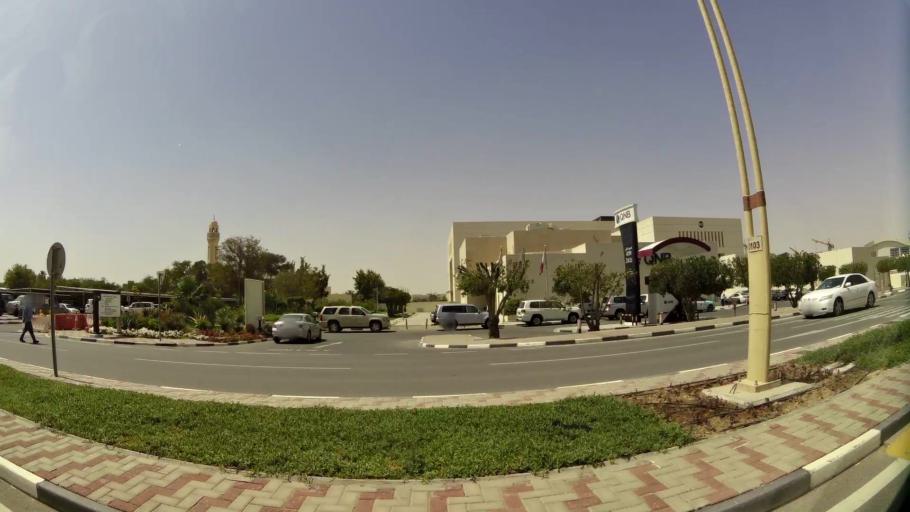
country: QA
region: Baladiyat Umm Salal
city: Umm Salal Muhammad
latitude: 25.3775
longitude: 51.4917
